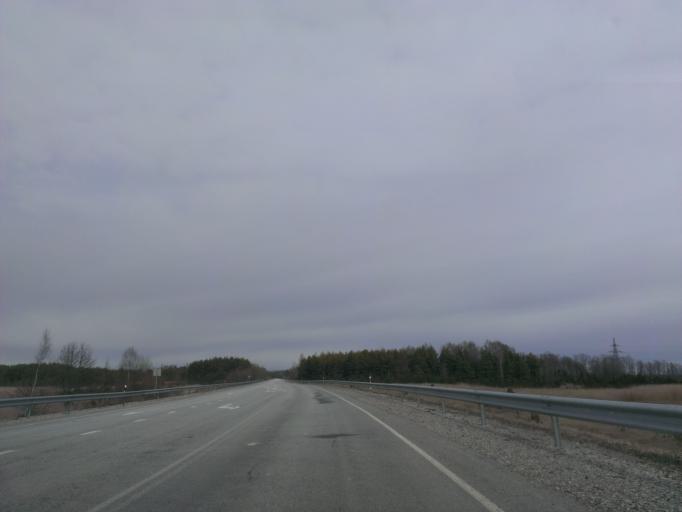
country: EE
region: Laeaene
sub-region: Lihula vald
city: Lihula
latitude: 58.5904
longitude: 23.5378
